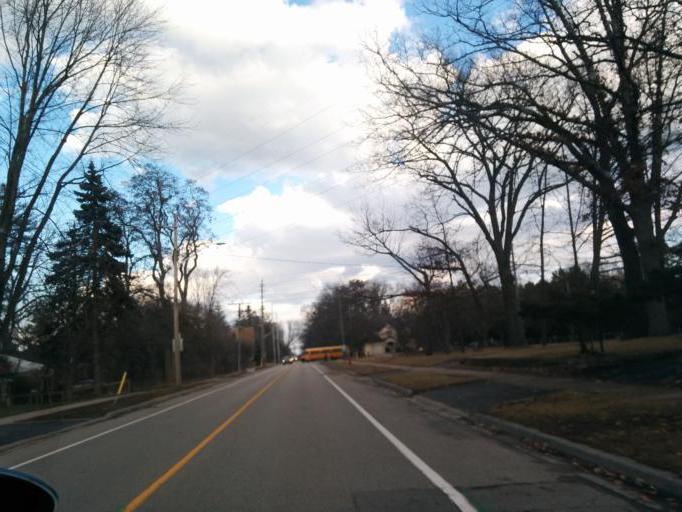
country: CA
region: Ontario
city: Mississauga
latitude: 43.5381
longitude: -79.6234
